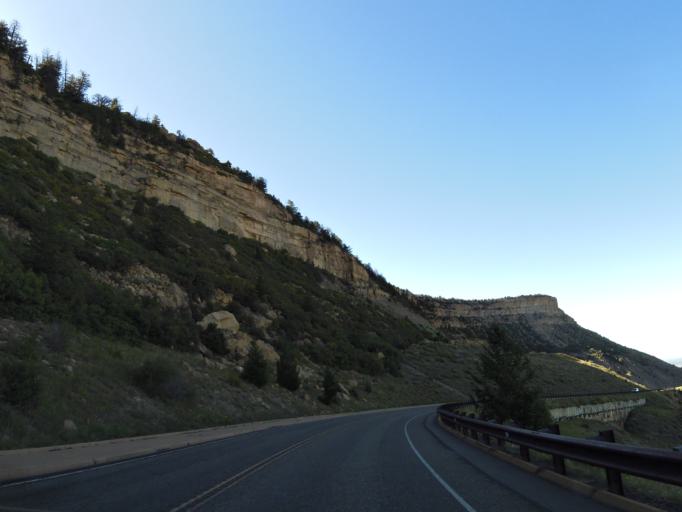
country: US
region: Colorado
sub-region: Montezuma County
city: Mancos
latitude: 37.3052
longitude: -108.4121
